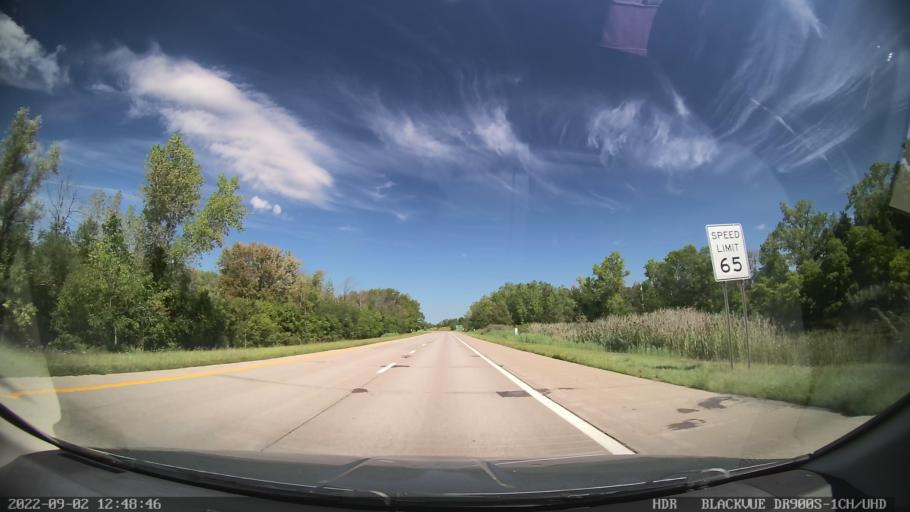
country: US
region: New York
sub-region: Livingston County
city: Livonia
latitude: 42.8385
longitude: -77.7322
